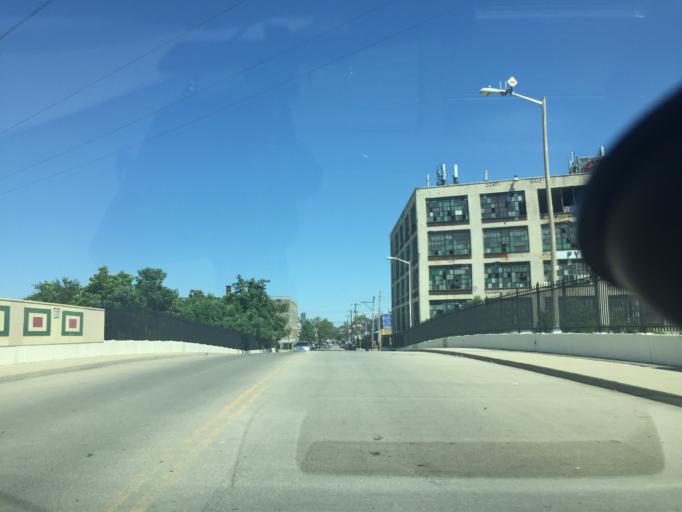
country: US
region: Pennsylvania
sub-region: Philadelphia County
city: Philadelphia
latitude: 39.9810
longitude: -75.1870
